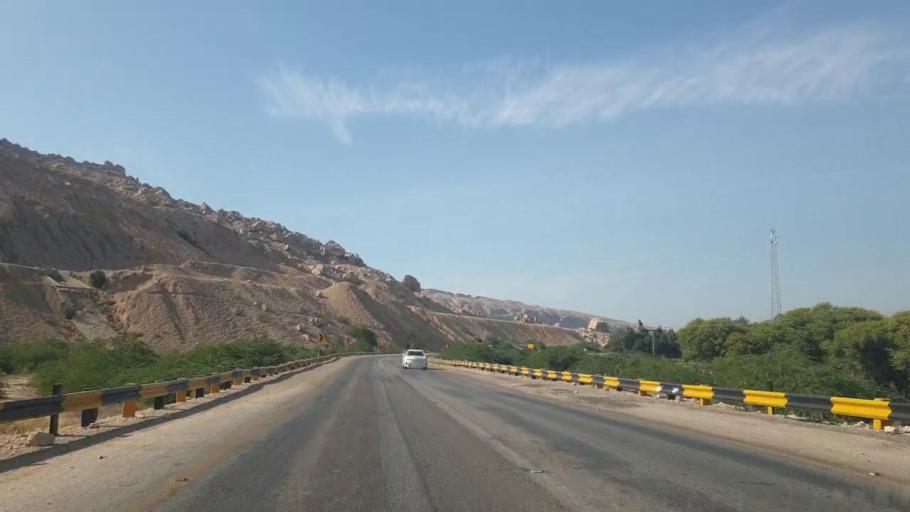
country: PK
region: Sindh
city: Sehwan
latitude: 26.3222
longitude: 67.8862
